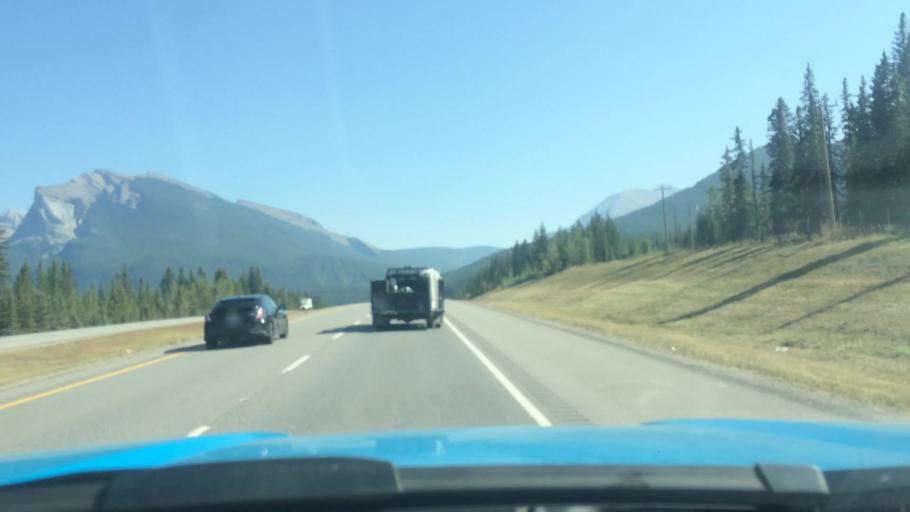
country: CA
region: Alberta
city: Canmore
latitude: 51.0470
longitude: -115.2948
